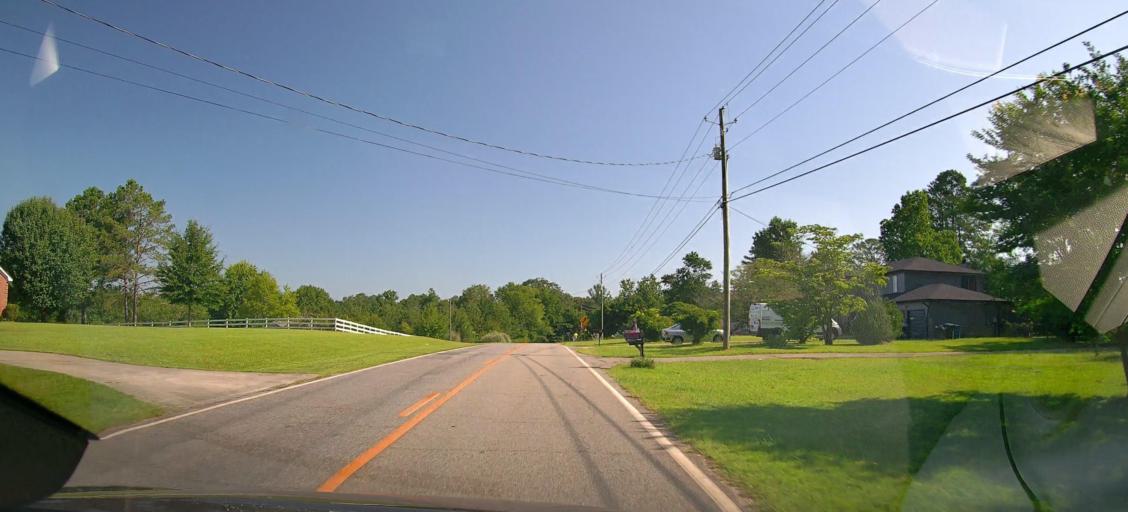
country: US
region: Georgia
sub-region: Peach County
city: Byron
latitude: 32.7257
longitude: -83.7095
